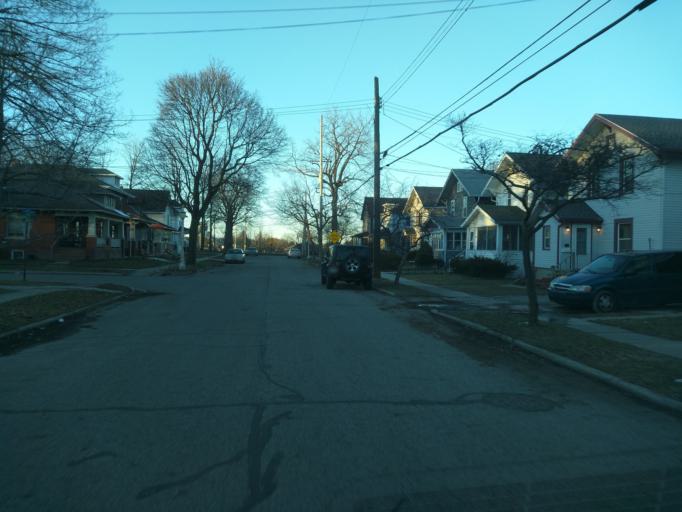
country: US
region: Michigan
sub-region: Ingham County
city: Lansing
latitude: 42.7356
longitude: -84.5273
